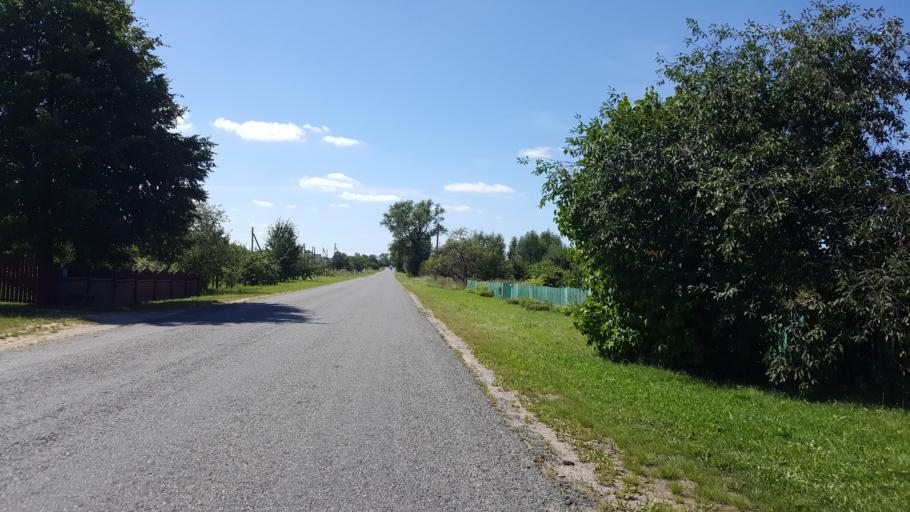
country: BY
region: Brest
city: Kamyanyets
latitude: 52.3730
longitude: 23.6296
